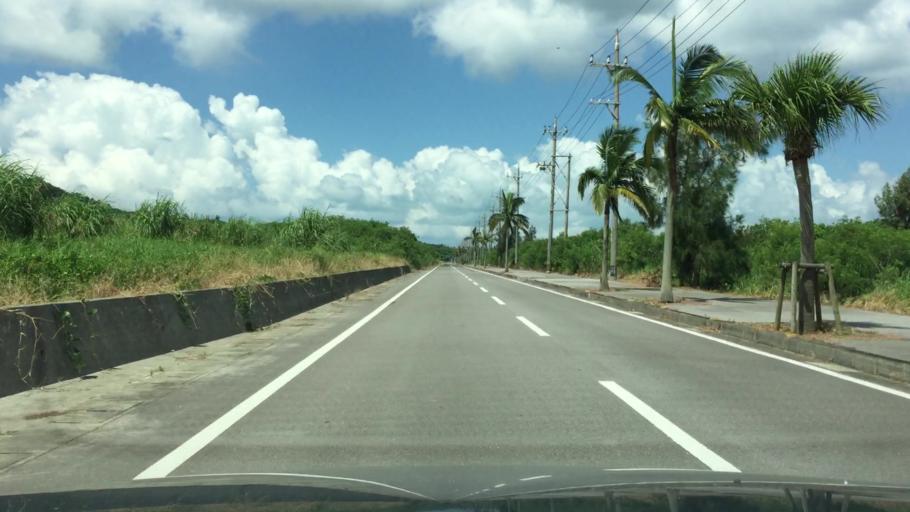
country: JP
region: Okinawa
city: Ishigaki
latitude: 24.3865
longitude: 124.1447
